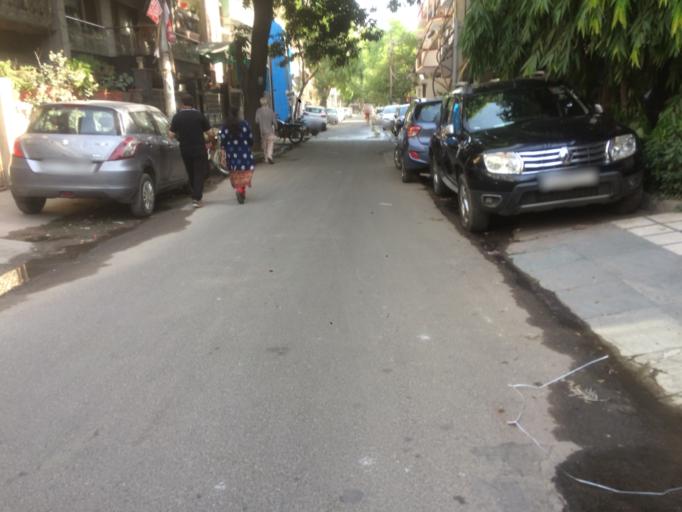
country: IN
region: Uttar Pradesh
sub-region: Gautam Buddha Nagar
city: Noida
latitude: 28.5603
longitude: 77.2574
